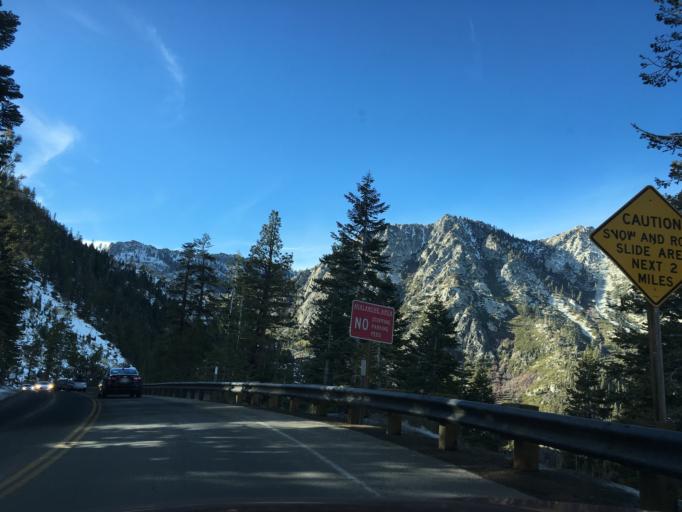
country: US
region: California
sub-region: El Dorado County
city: South Lake Tahoe
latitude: 38.9464
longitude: -120.0994
